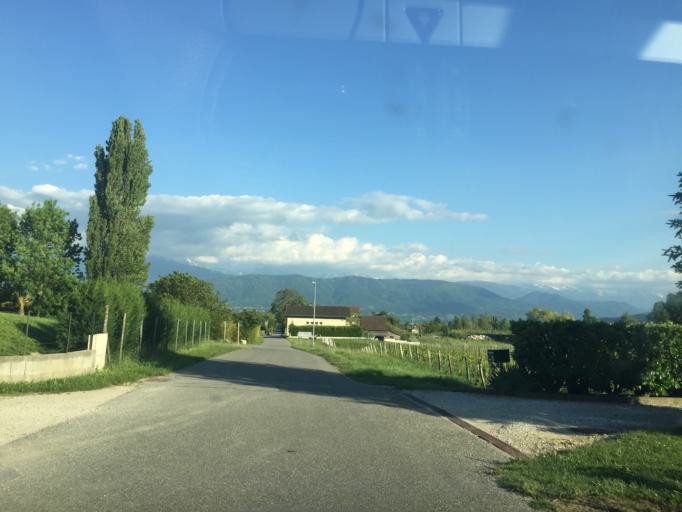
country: FR
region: Rhone-Alpes
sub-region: Departement de la Savoie
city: Les Marches
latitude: 45.5067
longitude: 5.9852
